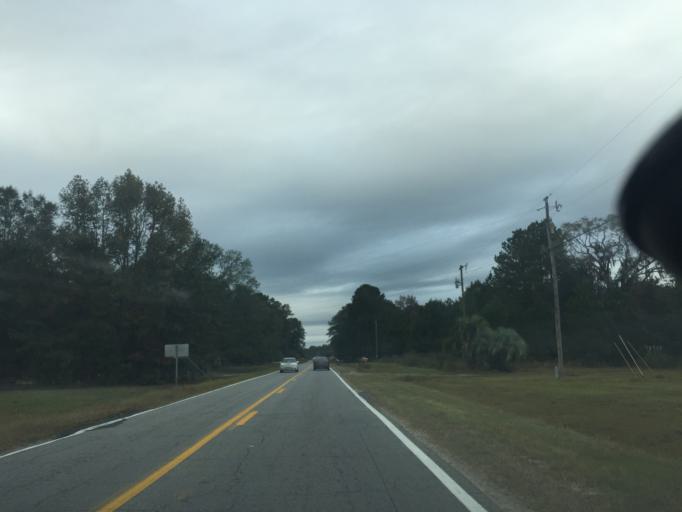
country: US
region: Georgia
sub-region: Chatham County
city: Bloomingdale
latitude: 32.0825
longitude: -81.3717
